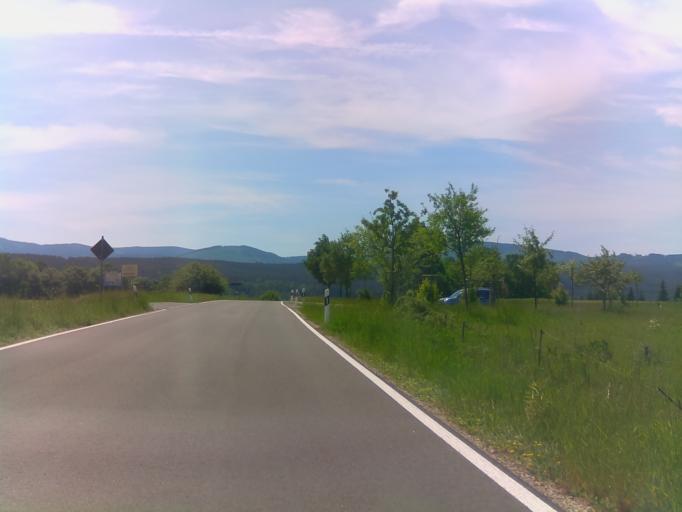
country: DE
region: Thuringia
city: Plaue
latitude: 50.7428
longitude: 10.9408
